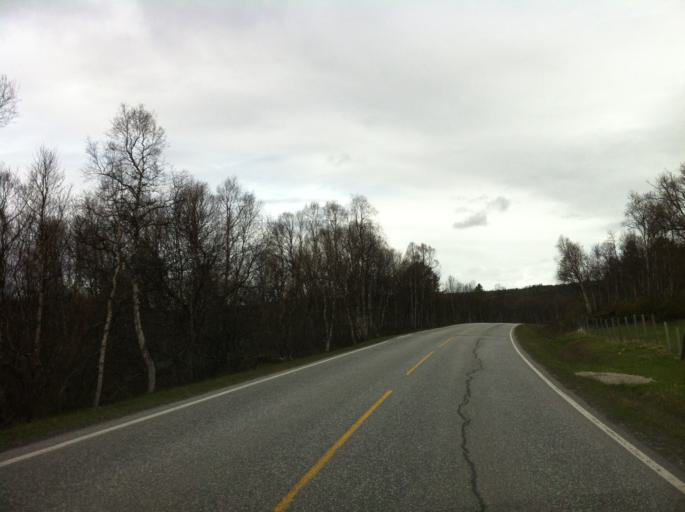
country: NO
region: Sor-Trondelag
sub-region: Roros
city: Roros
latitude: 62.5935
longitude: 11.4556
